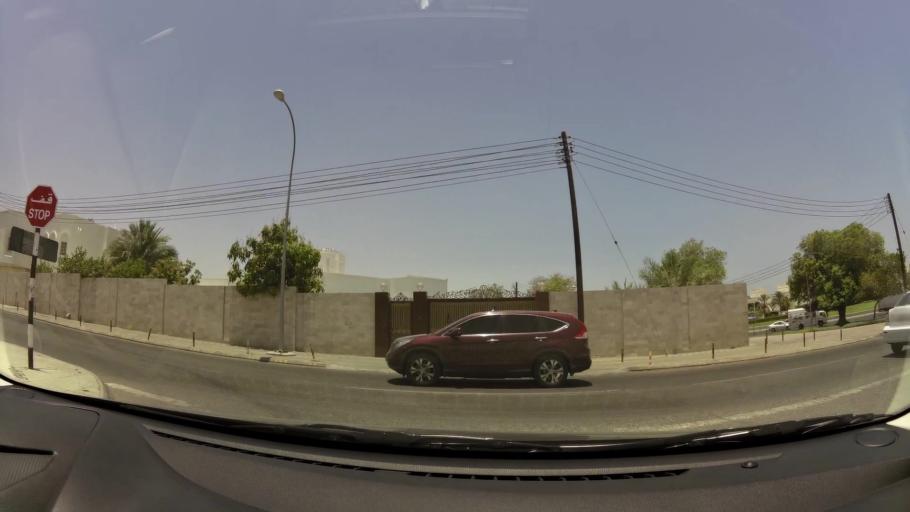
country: OM
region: Muhafazat Masqat
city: Bawshar
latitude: 23.6020
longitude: 58.4498
